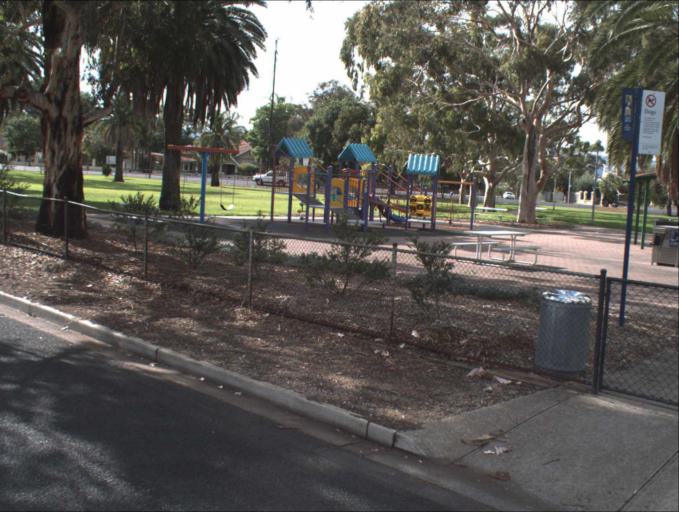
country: AU
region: South Australia
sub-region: Port Adelaide Enfield
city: Klemzig
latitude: -34.8800
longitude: 138.6238
